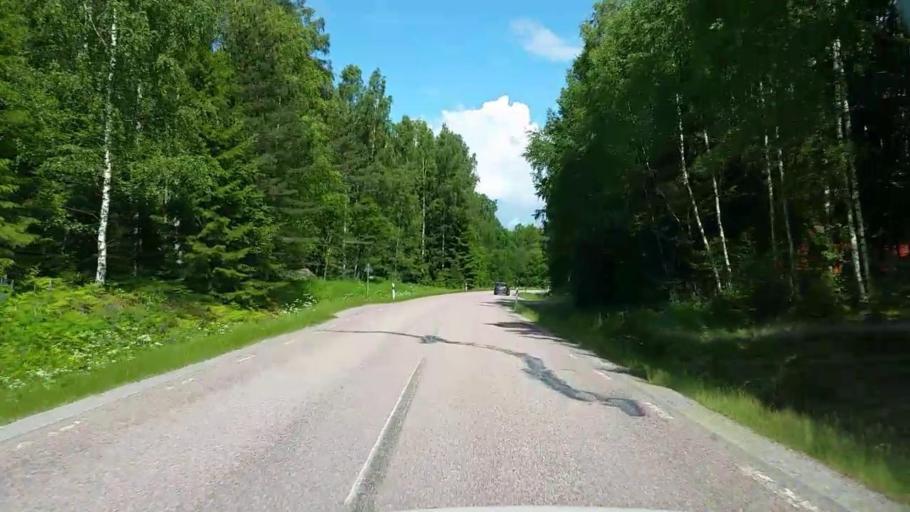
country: SE
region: Vaestmanland
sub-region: Fagersta Kommun
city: Fagersta
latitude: 59.9277
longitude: 15.8286
